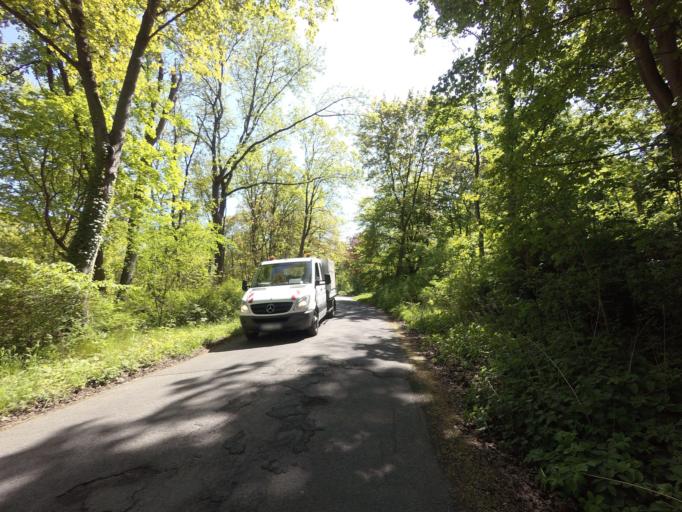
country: DE
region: Lower Saxony
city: Hildesheim
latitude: 52.1451
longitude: 9.9737
